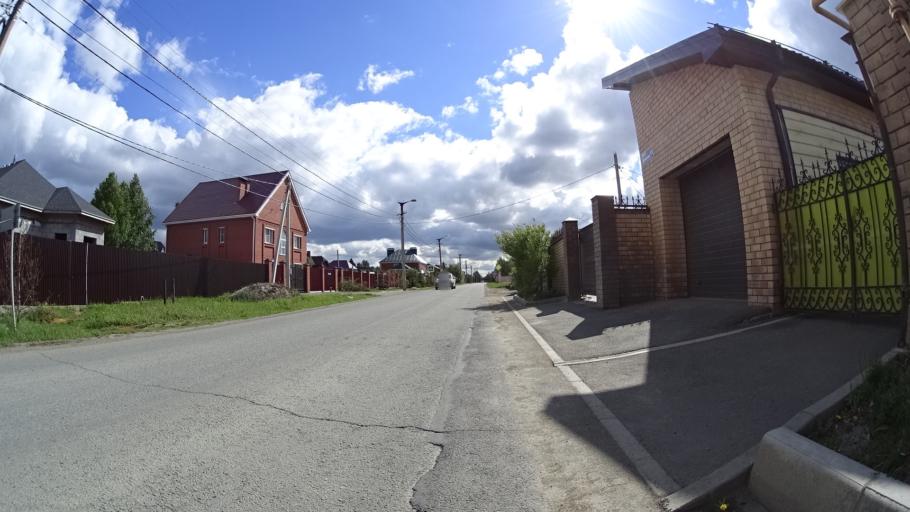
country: RU
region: Chelyabinsk
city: Sargazy
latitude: 55.1469
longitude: 61.2361
